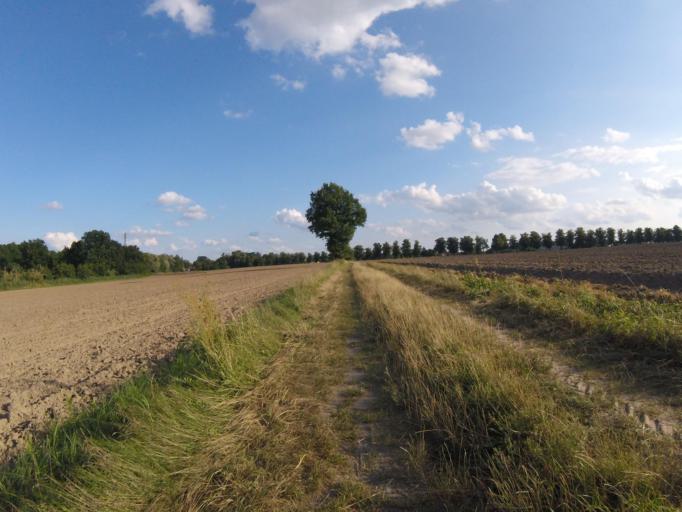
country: DE
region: Brandenburg
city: Mittenwalde
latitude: 52.2942
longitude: 13.5456
